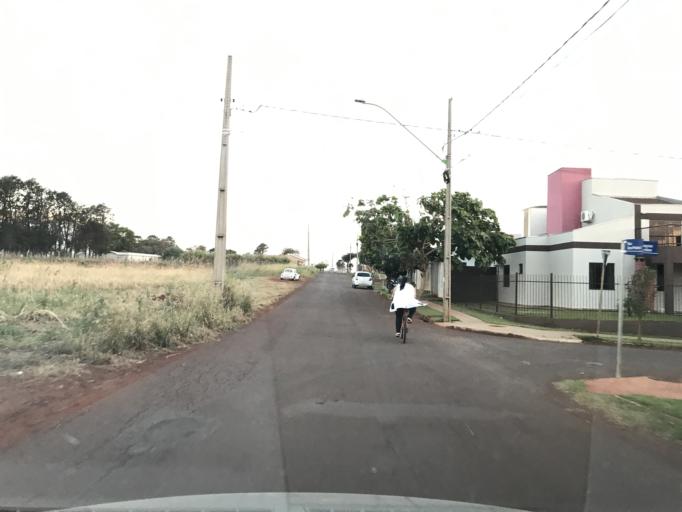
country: BR
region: Parana
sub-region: Palotina
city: Palotina
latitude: -24.3042
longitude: -53.8370
